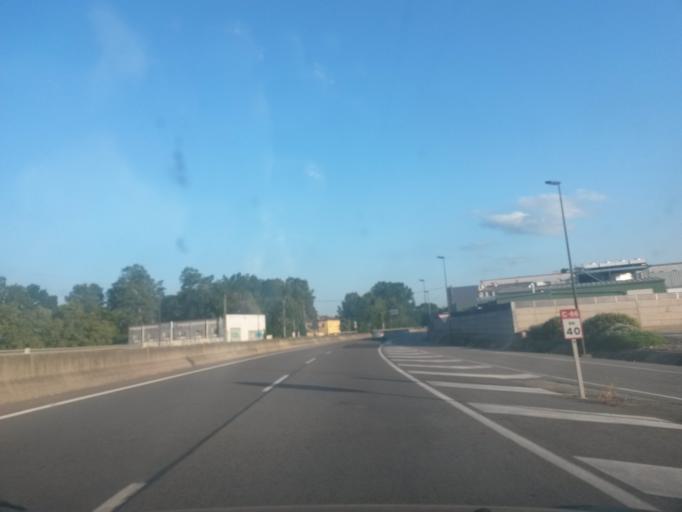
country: ES
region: Catalonia
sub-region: Provincia de Girona
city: Cornella del Terri
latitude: 42.0827
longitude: 2.8170
